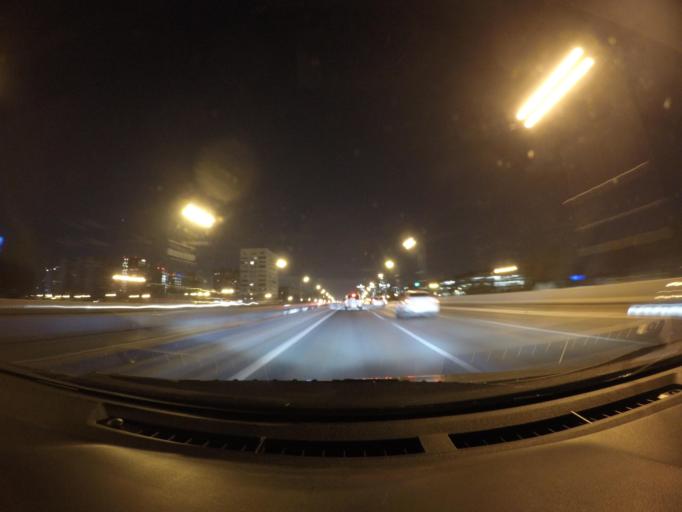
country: RU
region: Moskovskaya
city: Levoberezhnyy
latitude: 55.8399
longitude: 37.4809
